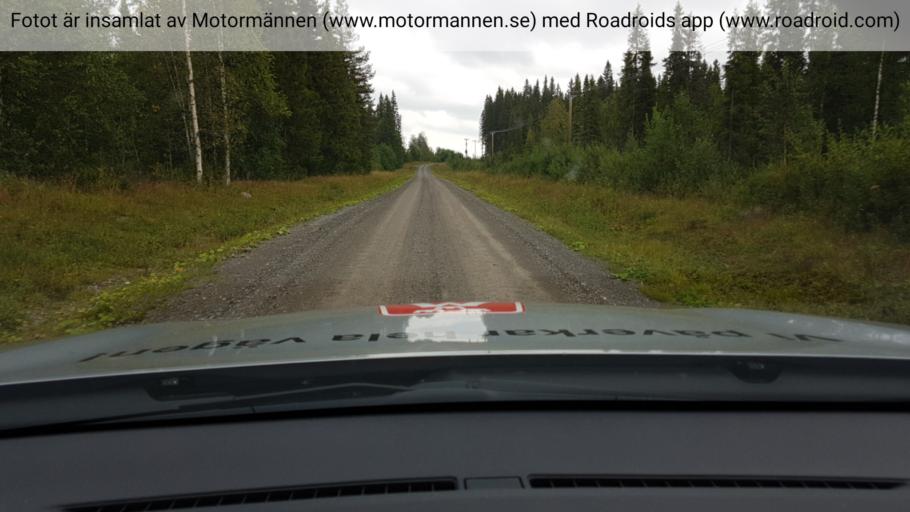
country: SE
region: Jaemtland
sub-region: Stroemsunds Kommun
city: Stroemsund
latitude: 63.7870
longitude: 15.2956
